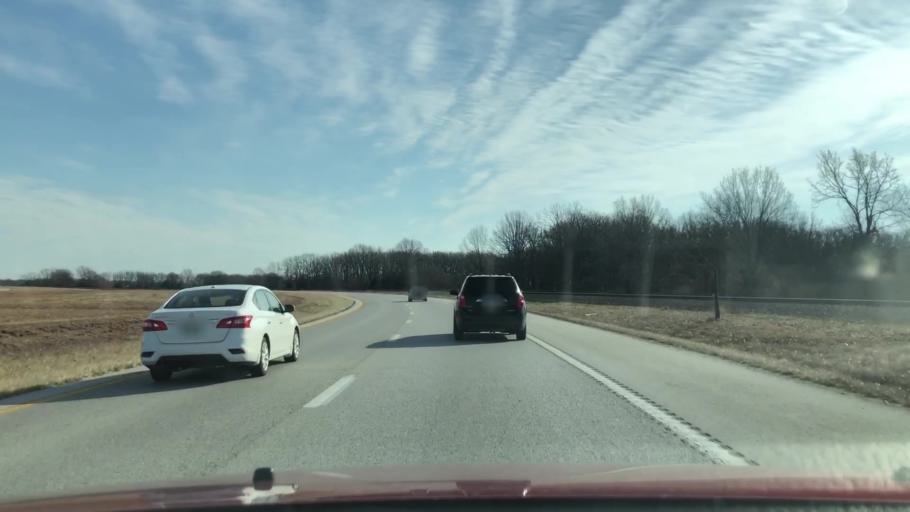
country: US
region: Missouri
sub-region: Webster County
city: Seymour
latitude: 37.1301
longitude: -92.7380
